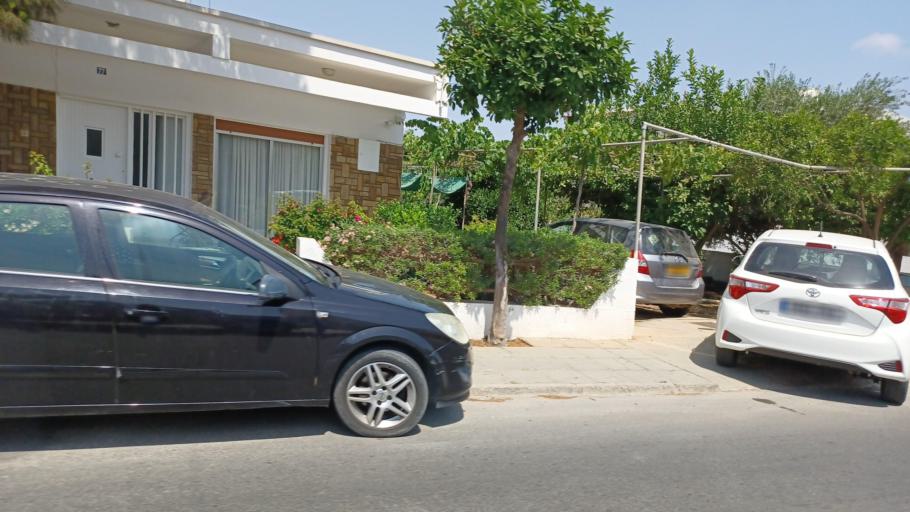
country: CY
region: Ammochostos
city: Paralimni
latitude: 35.0462
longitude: 33.9824
